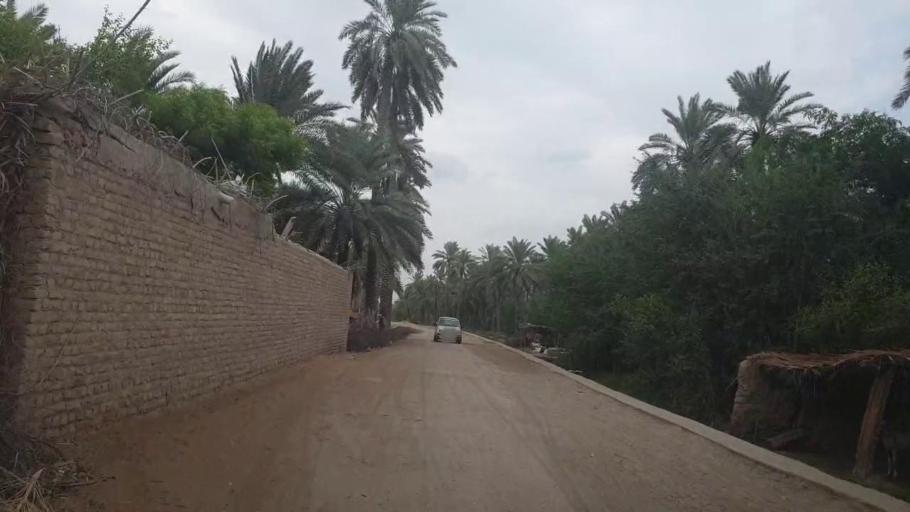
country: PK
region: Sindh
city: Khairpur
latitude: 27.5778
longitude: 68.7087
